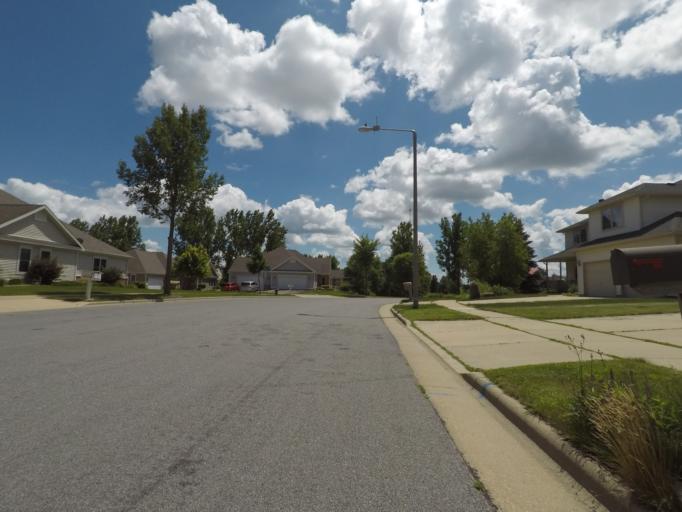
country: US
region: Wisconsin
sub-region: Dane County
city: Middleton
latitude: 43.0724
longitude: -89.5317
